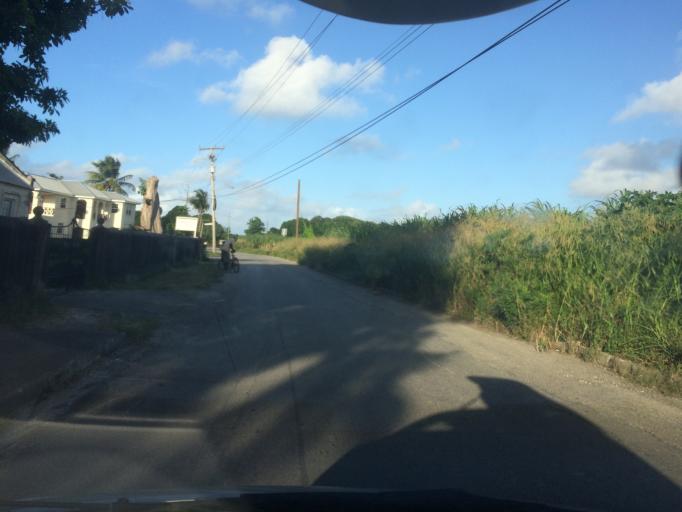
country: BB
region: Saint Lucy
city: Checker Hall
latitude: 13.3140
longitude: -59.6348
